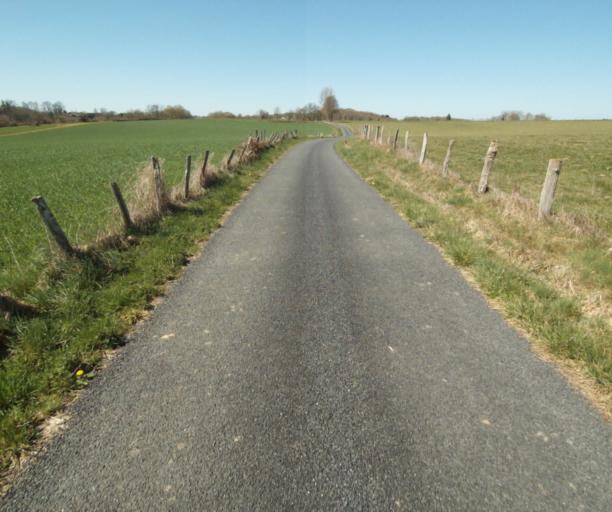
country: FR
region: Limousin
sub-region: Departement de la Correze
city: Chamboulive
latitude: 45.4572
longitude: 1.6956
